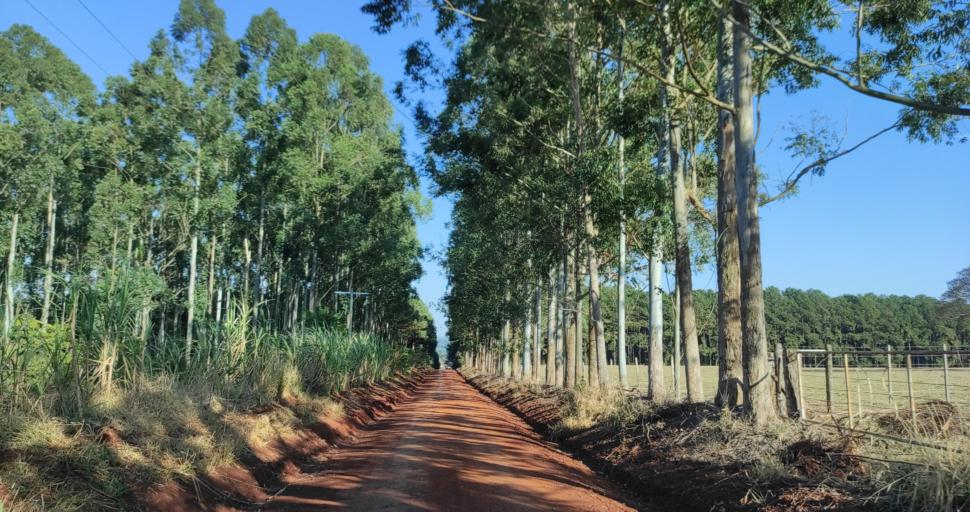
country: AR
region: Misiones
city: Puerto Rico
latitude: -26.8645
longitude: -55.0297
